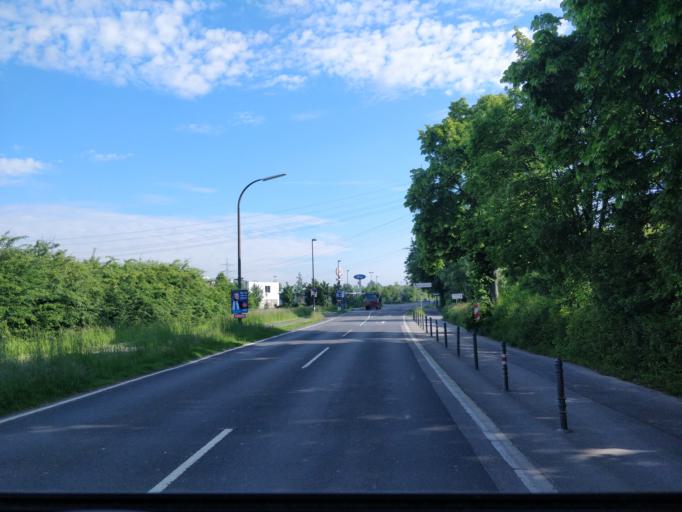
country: DE
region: North Rhine-Westphalia
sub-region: Regierungsbezirk Koln
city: Troisdorf
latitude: 50.8145
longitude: 7.1090
